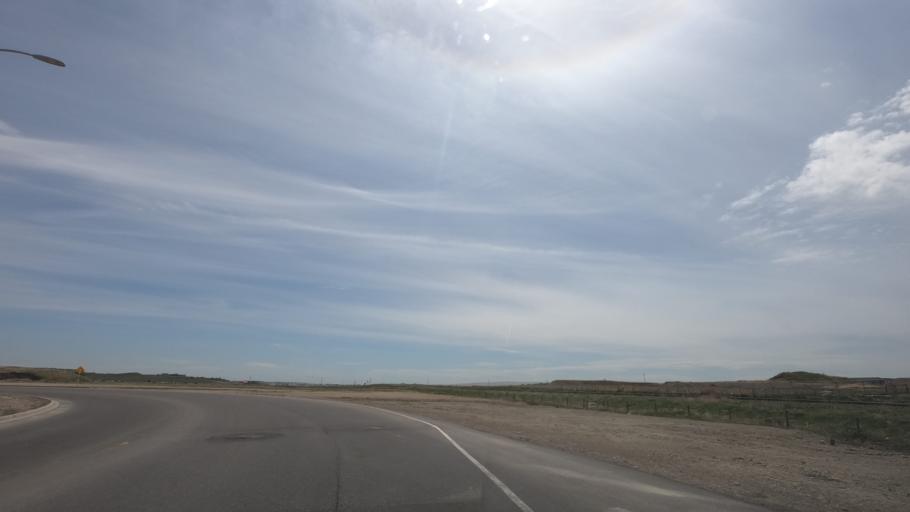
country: CA
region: Alberta
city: Airdrie
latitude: 51.2530
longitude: -114.0077
